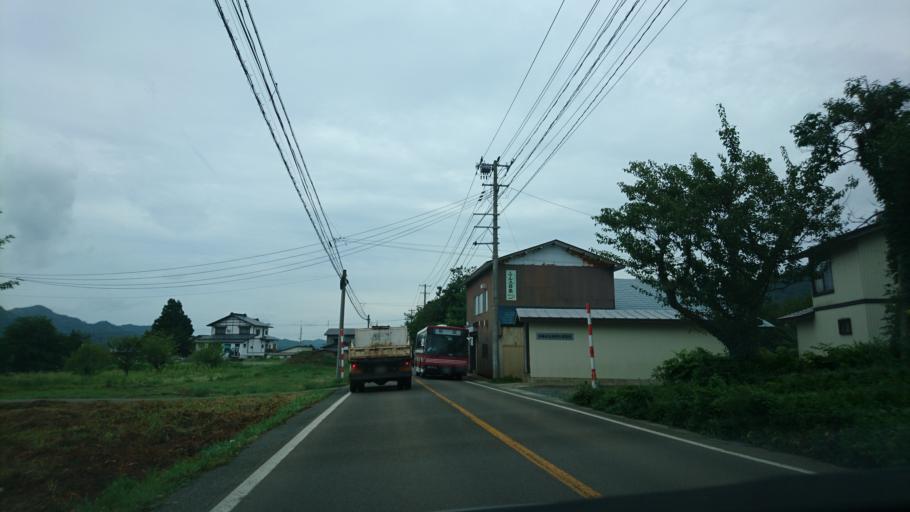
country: JP
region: Akita
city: Yuzawa
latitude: 39.1160
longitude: 140.5824
